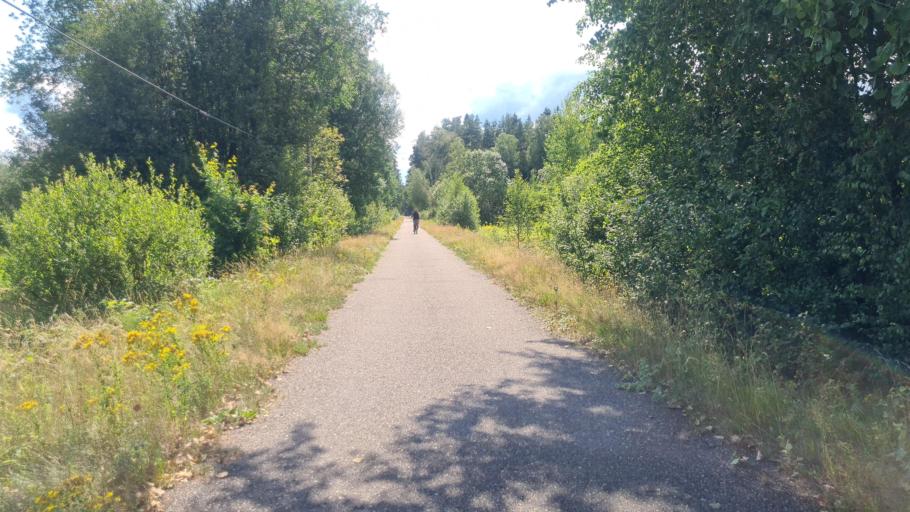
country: SE
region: Kronoberg
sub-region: Ljungby Kommun
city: Ljungby
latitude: 56.8486
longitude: 13.9666
